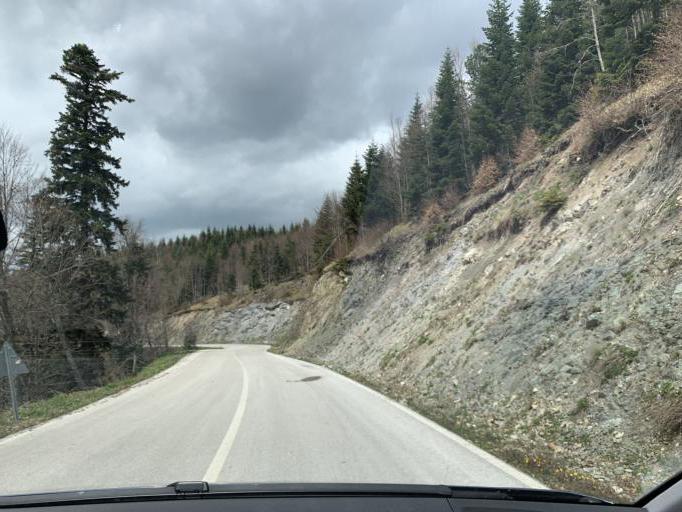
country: TR
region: Bolu
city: Bolu
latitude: 40.8943
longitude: 31.6714
